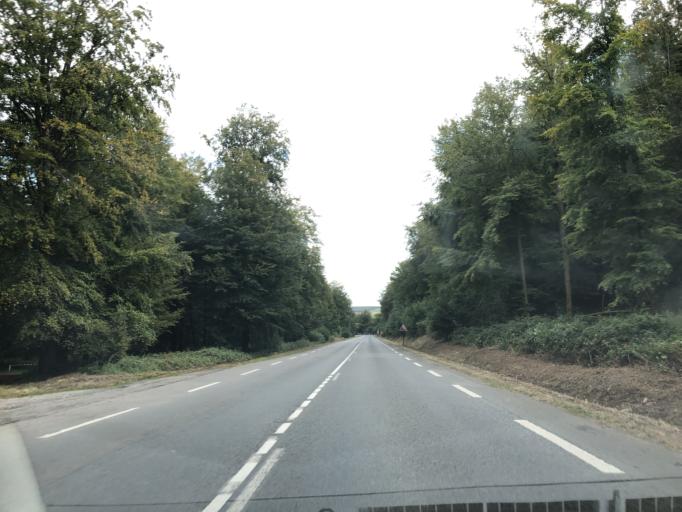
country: FR
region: Nord-Pas-de-Calais
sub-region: Departement du Pas-de-Calais
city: Hesdin
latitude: 50.3917
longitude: 2.0411
